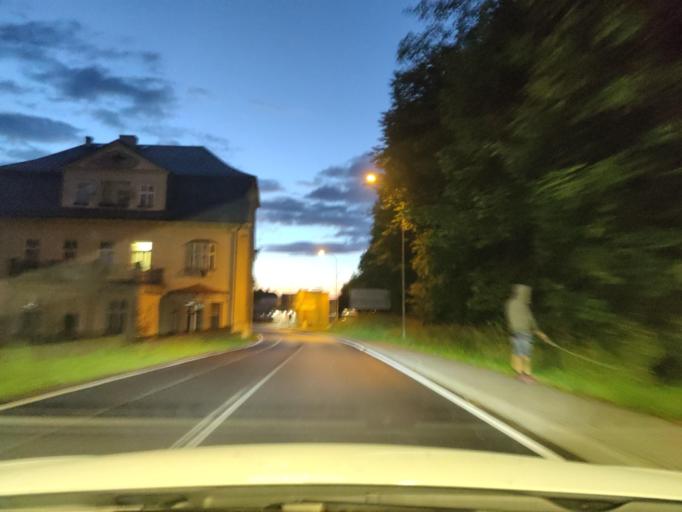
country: CZ
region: Olomoucky
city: Zlate Hory
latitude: 50.2600
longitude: 17.3983
